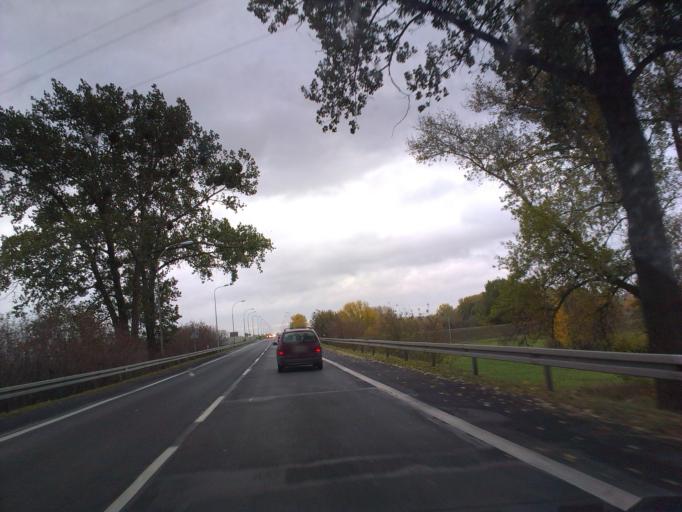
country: PL
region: Kujawsko-Pomorskie
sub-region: Powiat chelminski
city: Chelmno
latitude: 53.3763
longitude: 18.4210
